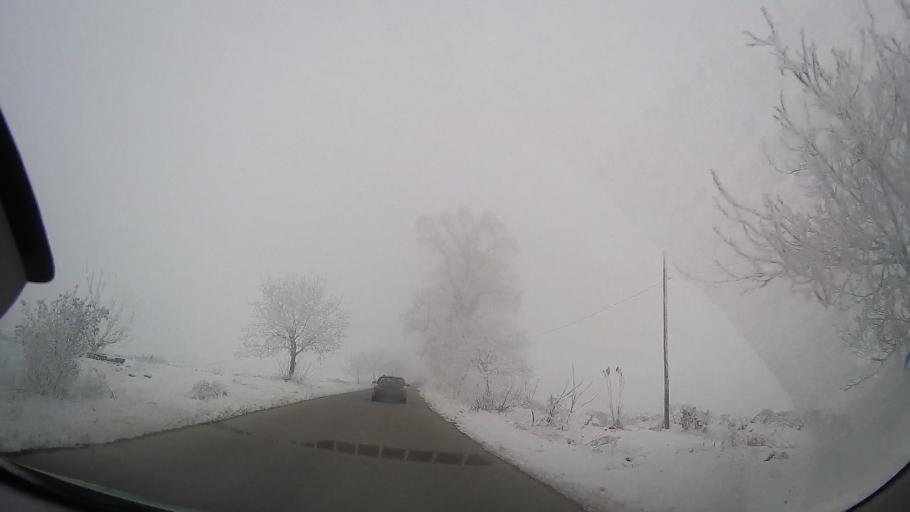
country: RO
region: Neamt
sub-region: Comuna Sabaoani
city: Sabaoani
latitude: 46.9900
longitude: 26.8629
